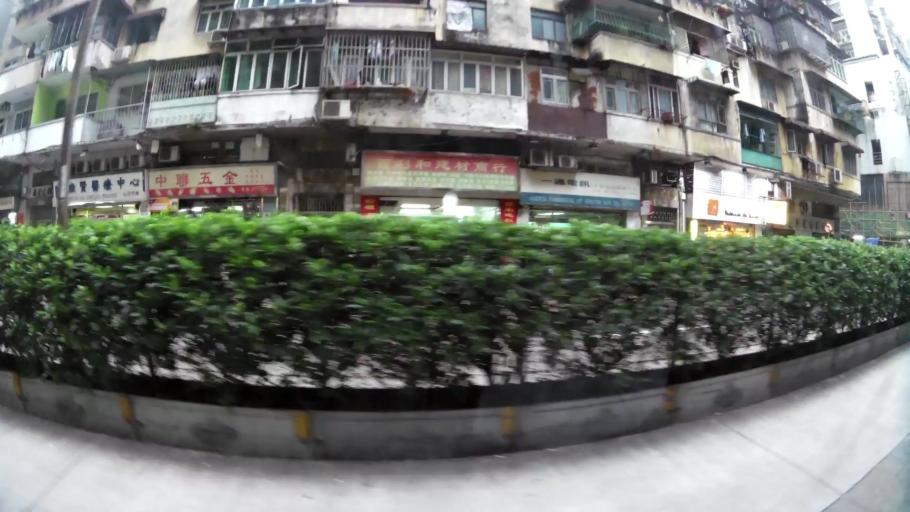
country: MO
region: Macau
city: Macau
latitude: 22.2044
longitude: 113.5432
